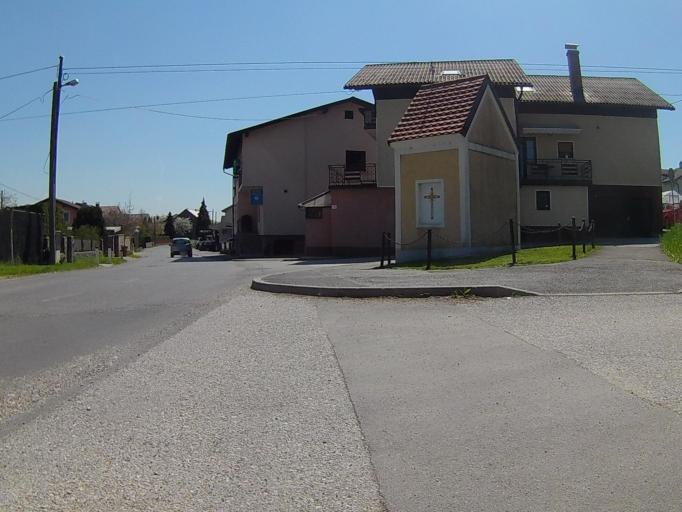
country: SI
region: Maribor
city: Razvanje
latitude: 46.5176
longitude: 15.6344
